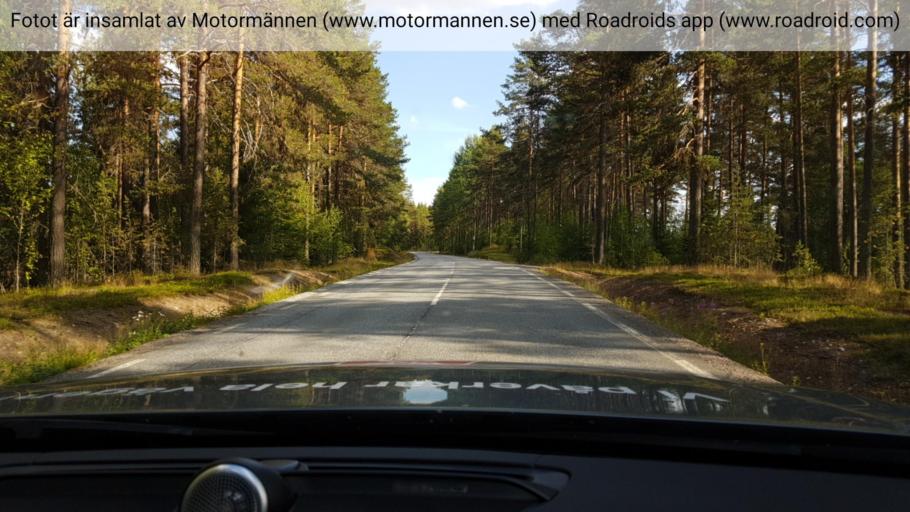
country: SE
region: Vaesterbotten
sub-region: Dorotea Kommun
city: Dorotea
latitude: 63.9132
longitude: 16.3481
